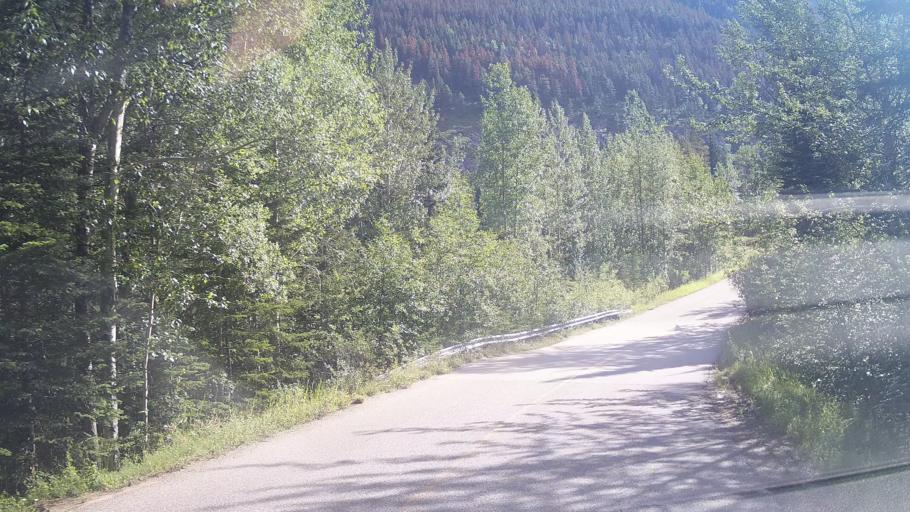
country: CA
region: Alberta
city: Hinton
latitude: 53.1782
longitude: -117.8370
